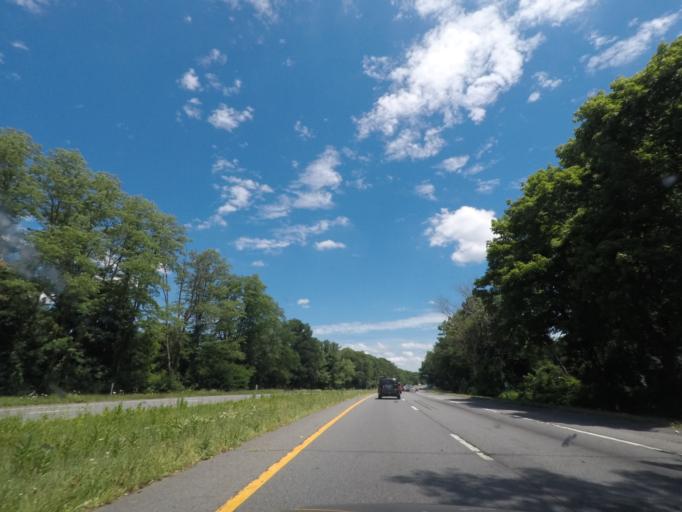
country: US
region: New York
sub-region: Schenectady County
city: Schenectady
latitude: 42.7904
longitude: -73.9061
